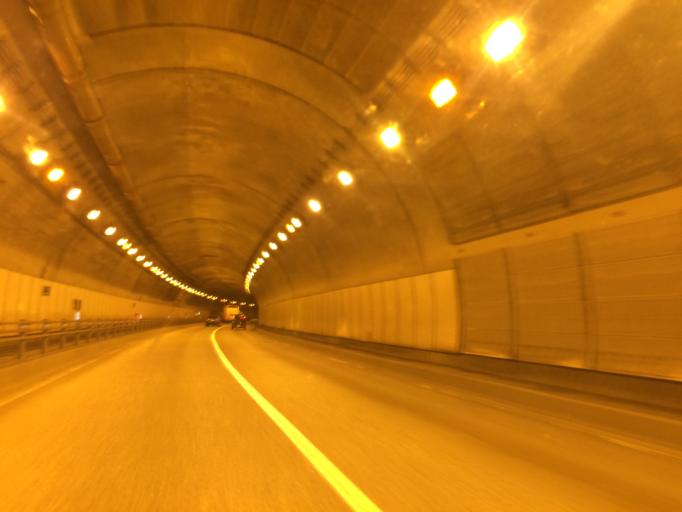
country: JP
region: Hokkaido
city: Otaru
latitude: 43.2062
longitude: 140.9725
